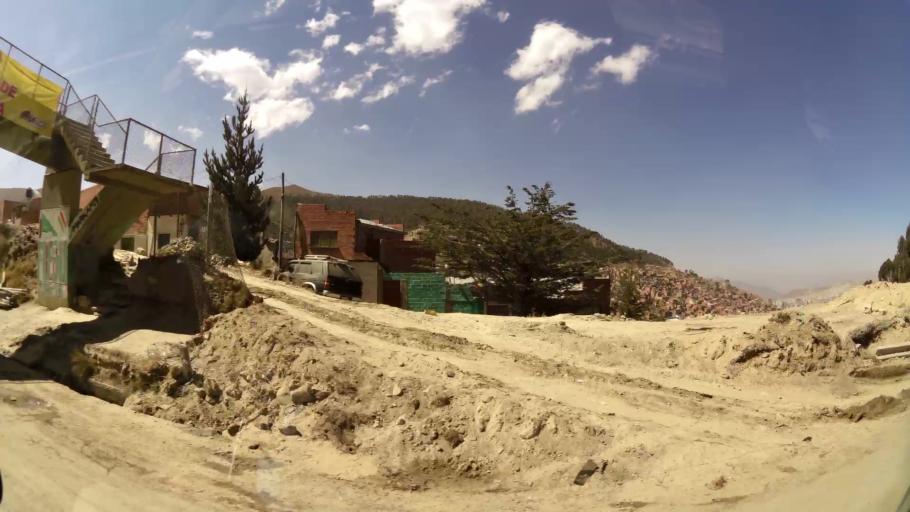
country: BO
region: La Paz
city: La Paz
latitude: -16.4673
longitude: -68.1557
